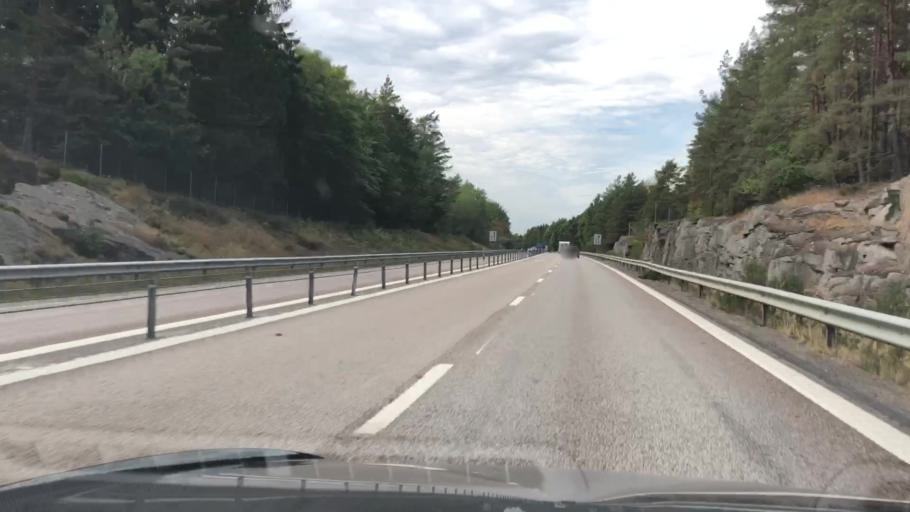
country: SE
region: Blekinge
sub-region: Ronneby Kommun
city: Brakne-Hoby
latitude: 56.2211
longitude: 15.1463
